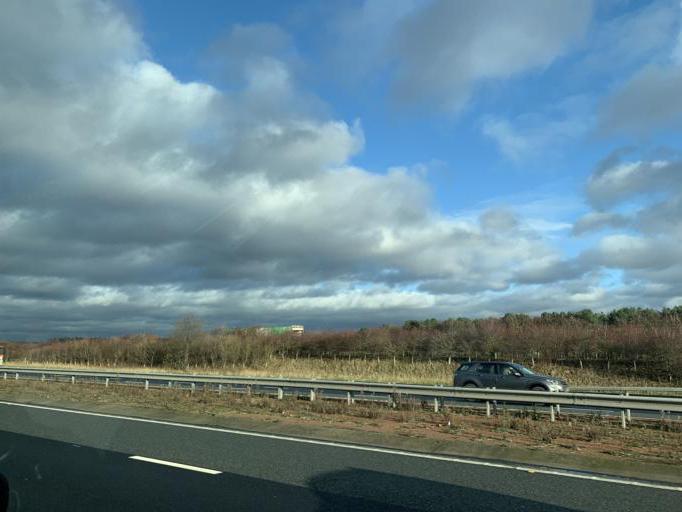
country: GB
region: England
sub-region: City and Borough of Leeds
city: Ledsham
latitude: 53.7866
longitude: -1.3222
